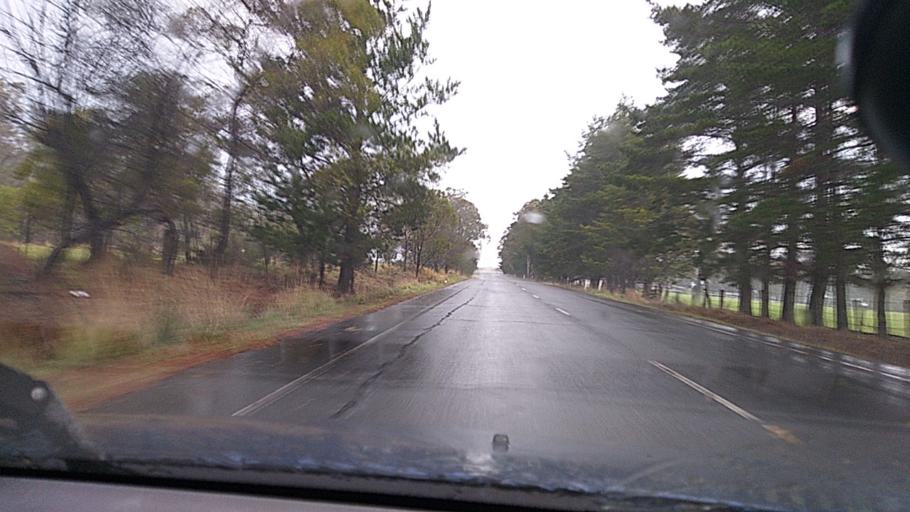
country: AU
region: New South Wales
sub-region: Wollondilly
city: Douglas Park
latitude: -34.2550
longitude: 150.7231
